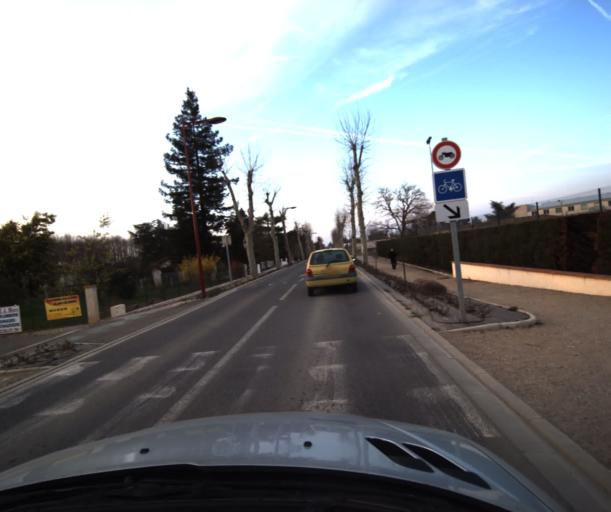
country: FR
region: Midi-Pyrenees
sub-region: Departement du Tarn-et-Garonne
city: Labastide-Saint-Pierre
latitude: 43.9136
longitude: 1.3685
